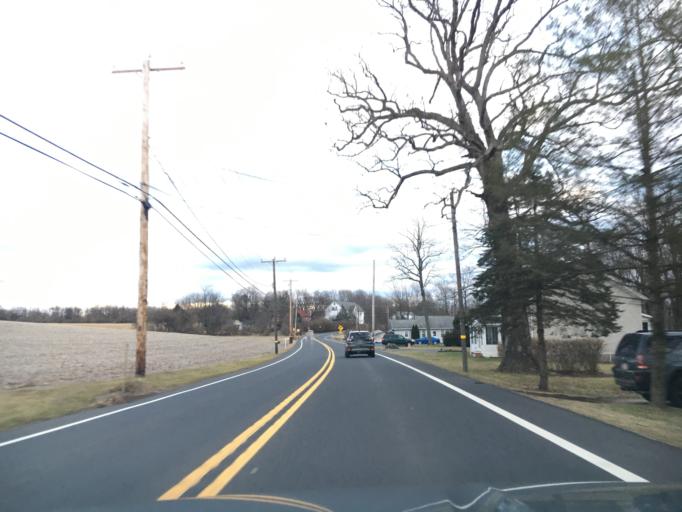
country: US
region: Pennsylvania
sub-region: Lehigh County
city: Schnecksville
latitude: 40.6826
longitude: -75.6601
